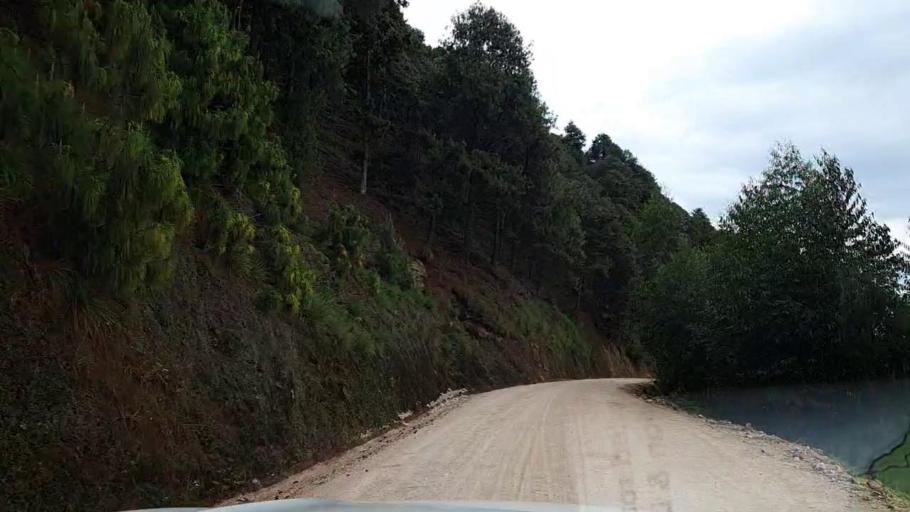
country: RW
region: Southern Province
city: Nzega
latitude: -2.4068
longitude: 29.4542
